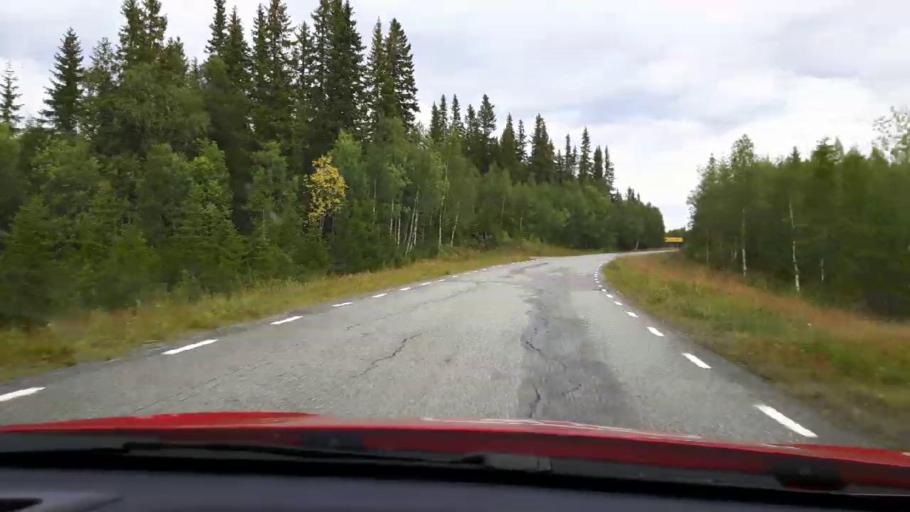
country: SE
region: Jaemtland
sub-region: Are Kommun
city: Are
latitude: 63.7142
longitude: 12.9606
